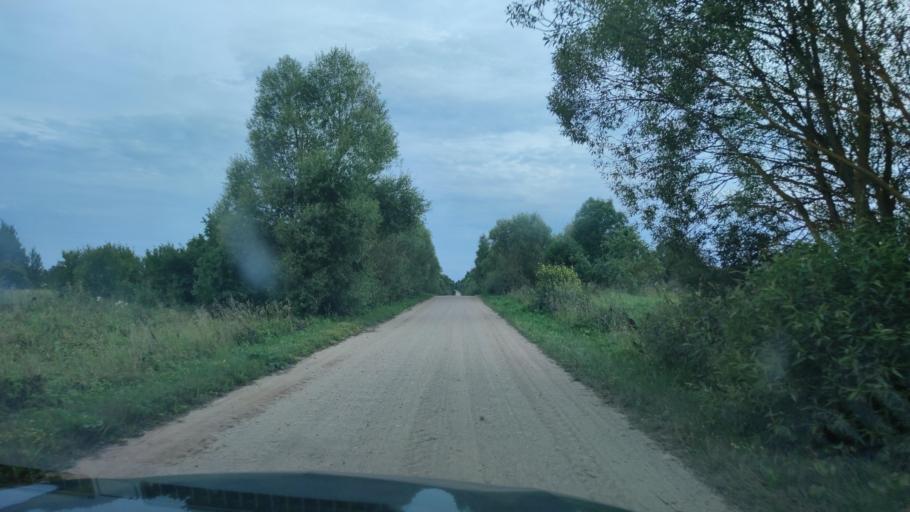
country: BY
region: Vitebsk
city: Pastavy
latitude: 55.1223
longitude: 27.1540
